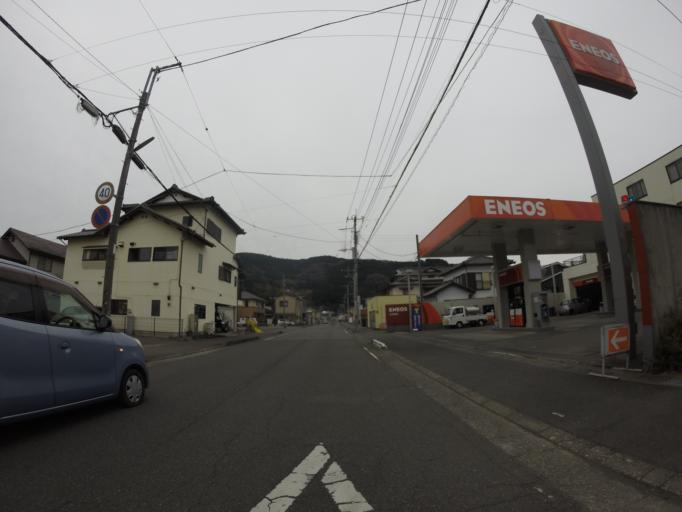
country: JP
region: Shizuoka
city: Fujinomiya
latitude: 35.2262
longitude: 138.5954
